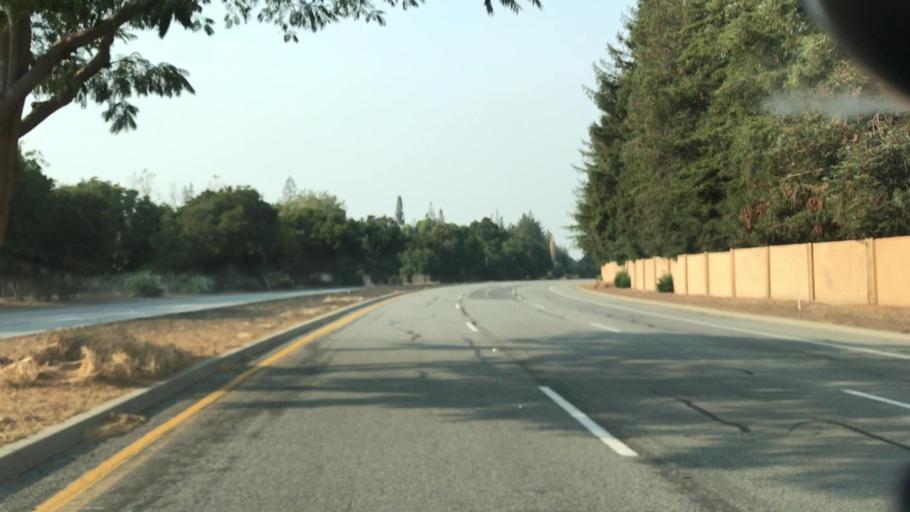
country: US
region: California
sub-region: Santa Clara County
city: Cupertino
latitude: 37.2987
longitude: -121.9974
